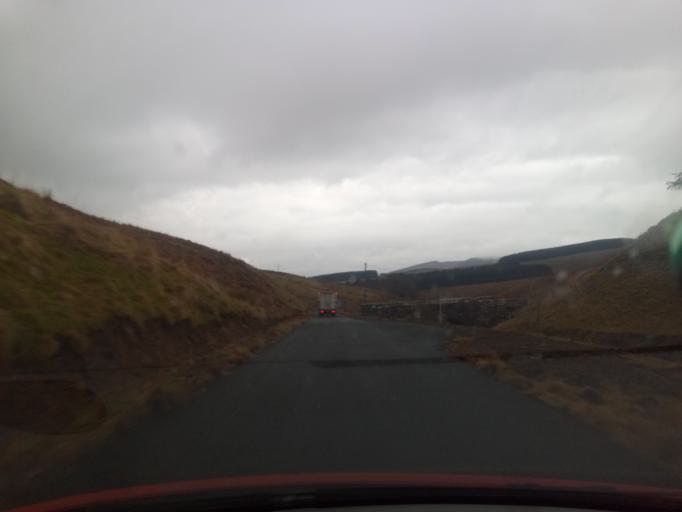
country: GB
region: Scotland
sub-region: The Scottish Borders
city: Hawick
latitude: 55.2751
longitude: -2.6820
